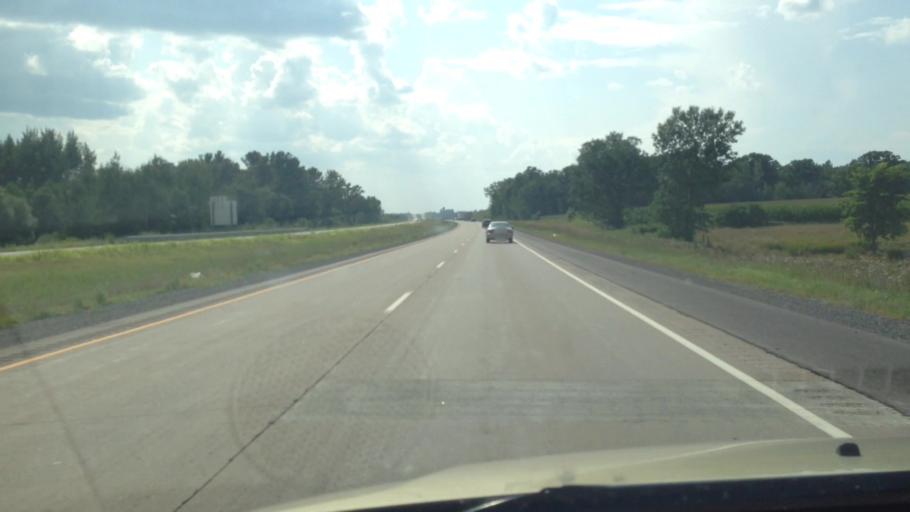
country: US
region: Wisconsin
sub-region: Clark County
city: Thorp
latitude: 44.9522
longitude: -90.8242
